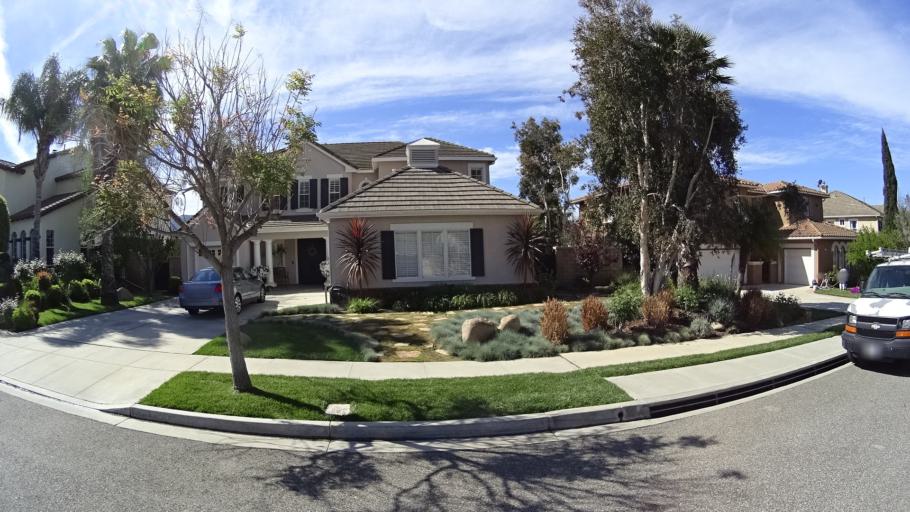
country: US
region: California
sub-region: Ventura County
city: Casa Conejo
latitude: 34.1738
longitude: -118.9666
